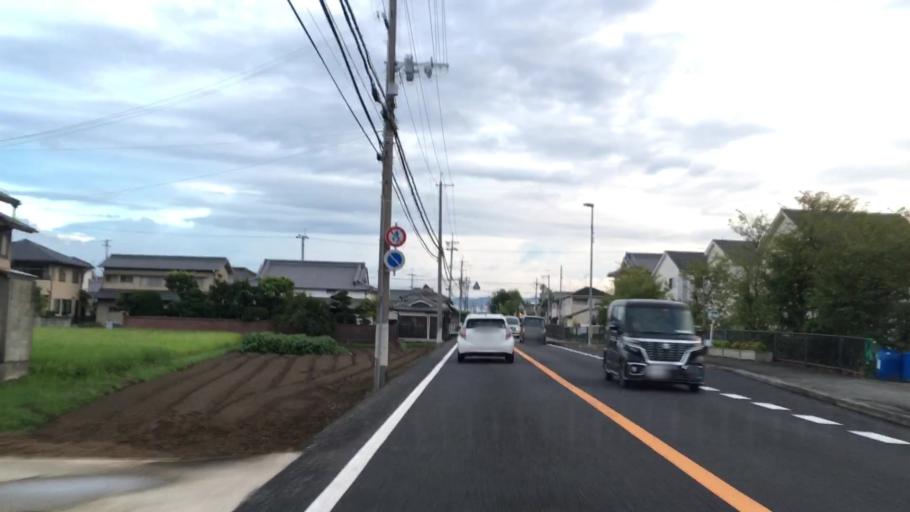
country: JP
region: Hyogo
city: Himeji
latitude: 34.9023
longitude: 134.7356
